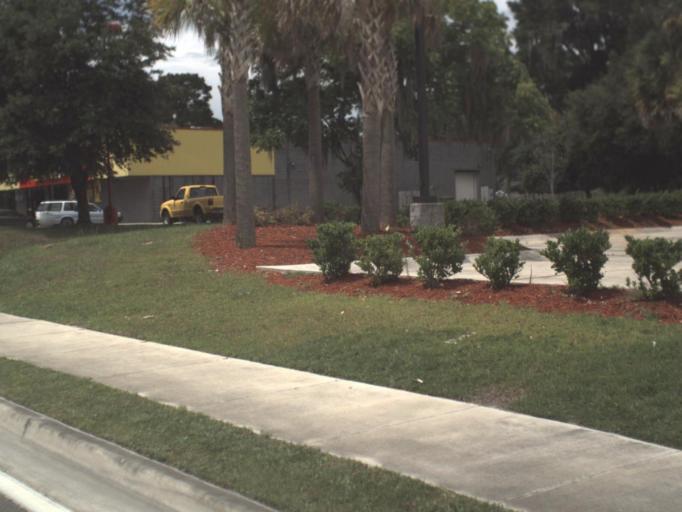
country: US
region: Florida
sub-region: Suwannee County
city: Live Oak
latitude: 30.2878
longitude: -82.9878
